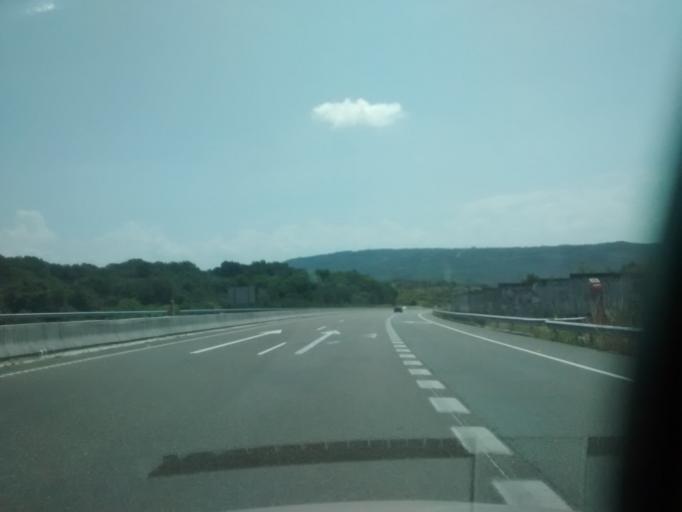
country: ES
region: Galicia
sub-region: Provincia de Ourense
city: Maside
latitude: 42.3996
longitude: -8.0034
